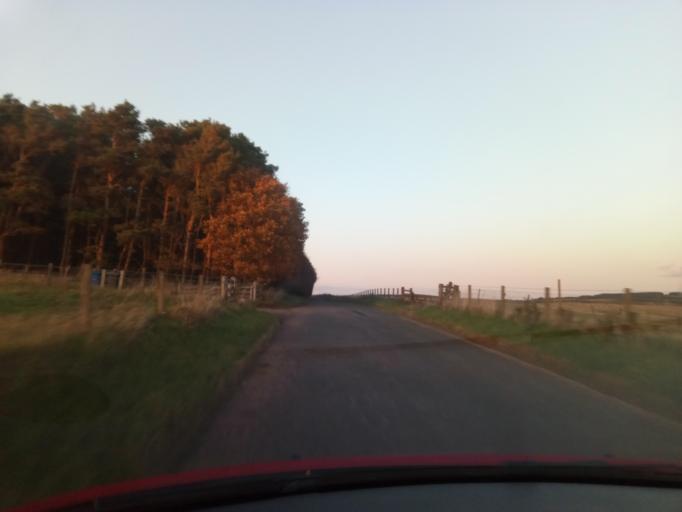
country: GB
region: Scotland
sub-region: East Lothian
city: Pencaitland
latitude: 55.8131
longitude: -2.8759
